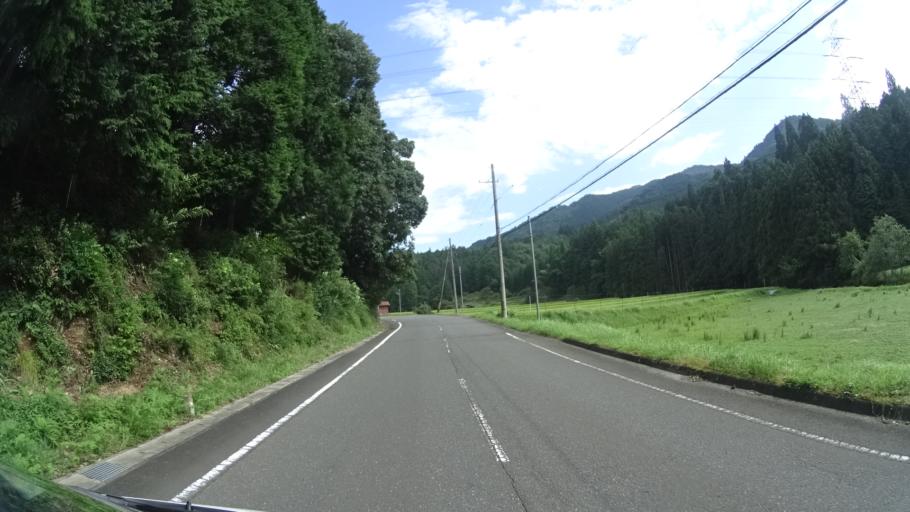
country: JP
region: Kyoto
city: Fukuchiyama
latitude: 35.3600
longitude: 135.1385
